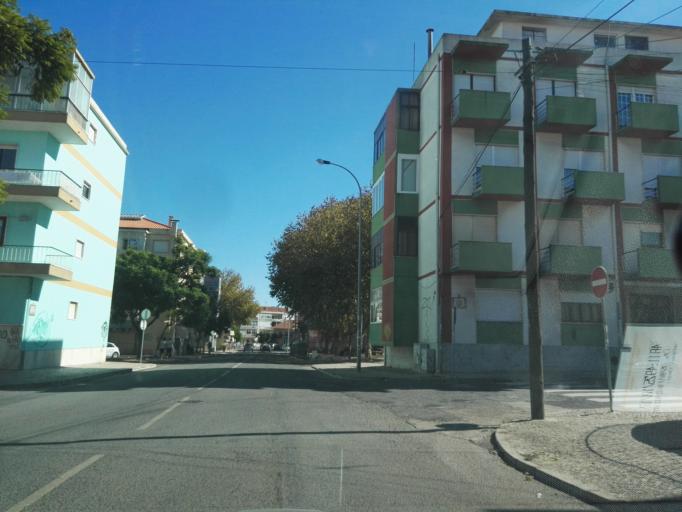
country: PT
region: Lisbon
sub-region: Sintra
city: Sintra
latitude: 38.7973
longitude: -9.3494
